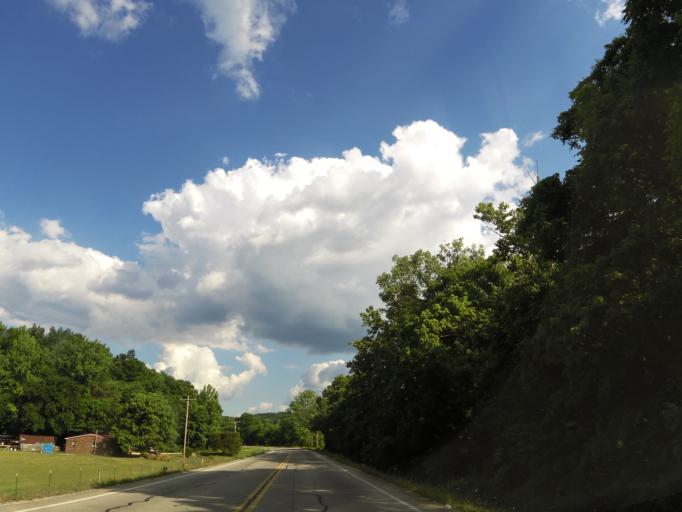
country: US
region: Tennessee
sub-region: Perry County
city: Linden
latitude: 35.6198
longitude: -87.7334
